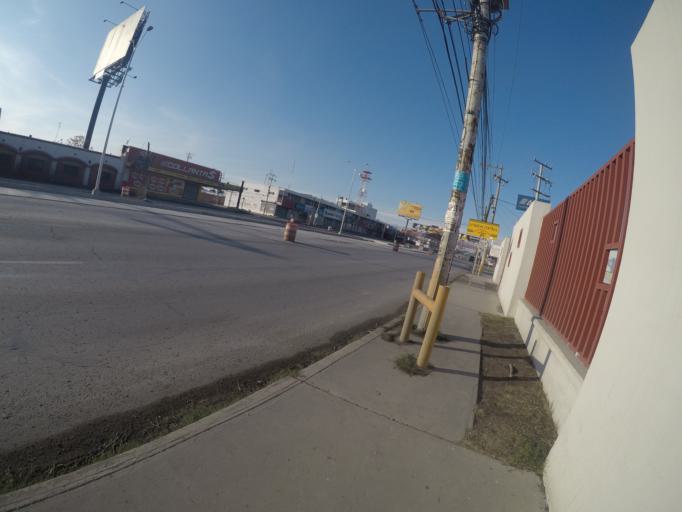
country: MX
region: Chihuahua
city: Ciudad Juarez
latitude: 31.7205
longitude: -106.4242
